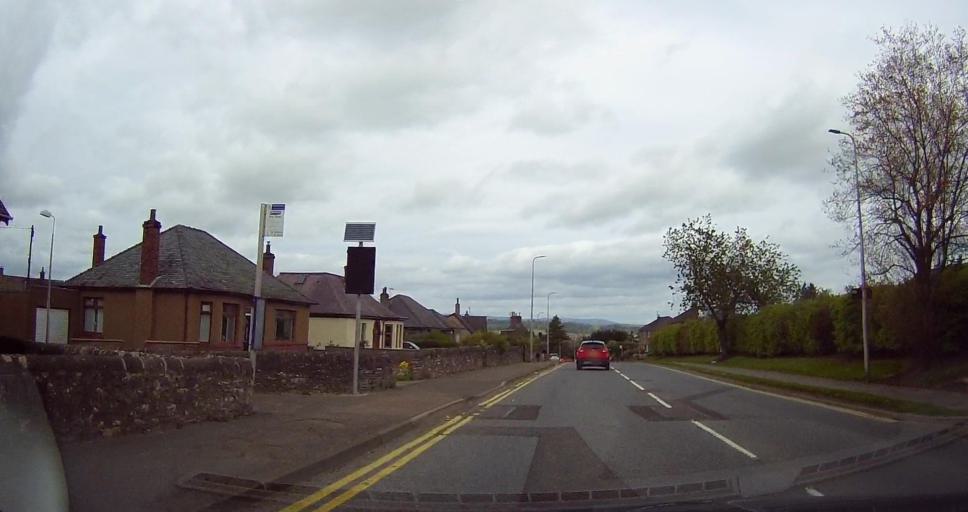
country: GB
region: Scotland
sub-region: Angus
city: Forfar
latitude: 56.6348
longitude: -2.8954
